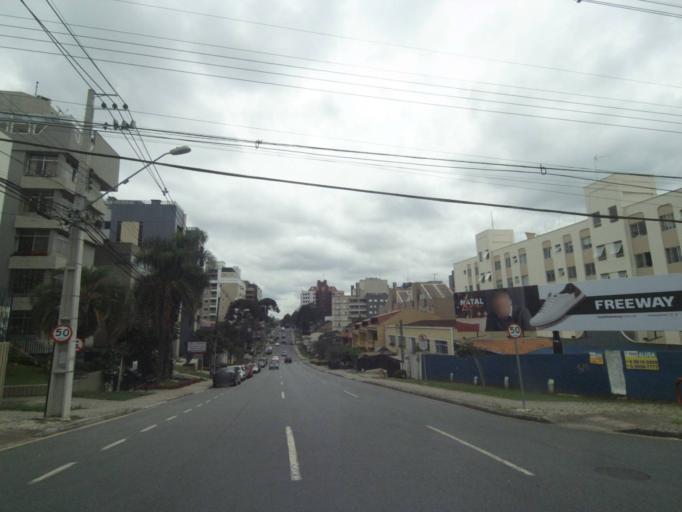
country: BR
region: Parana
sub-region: Curitiba
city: Curitiba
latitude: -25.4340
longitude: -49.2955
